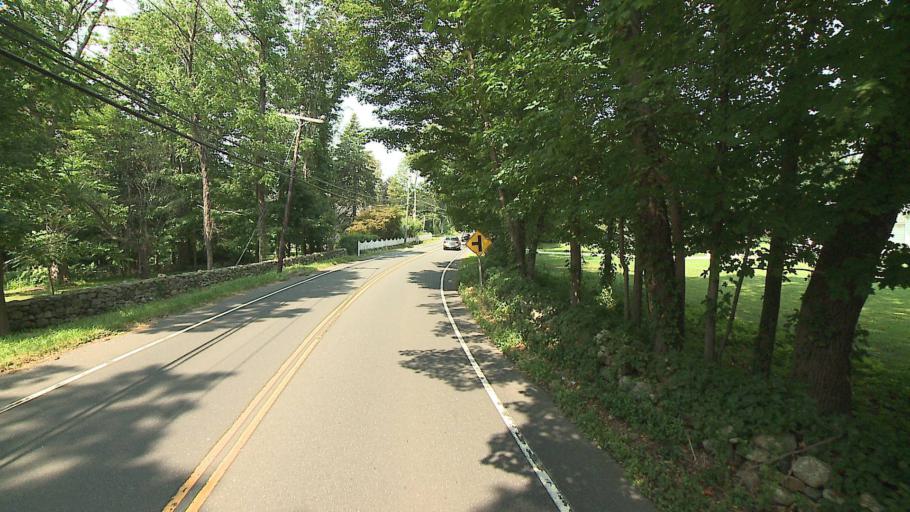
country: US
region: Connecticut
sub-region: Fairfield County
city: Ridgefield
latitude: 41.3194
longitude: -73.5186
